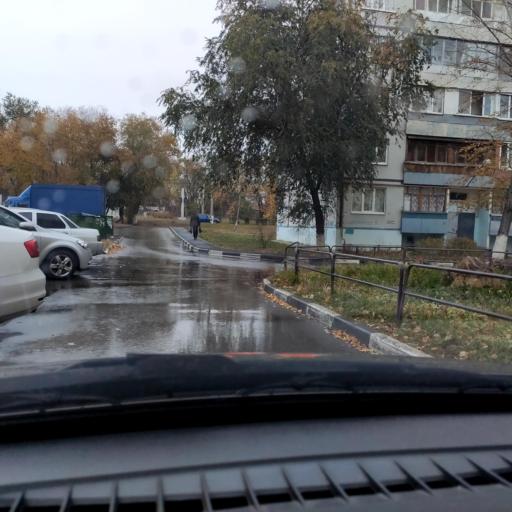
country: RU
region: Samara
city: Zhigulevsk
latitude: 53.4783
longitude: 49.4849
